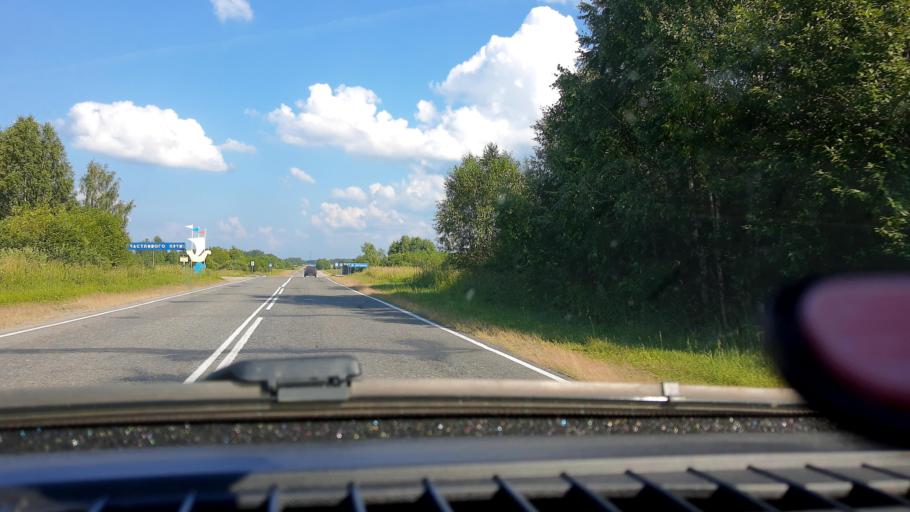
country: RU
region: Nizjnij Novgorod
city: Neklyudovo
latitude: 56.5061
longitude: 43.9733
